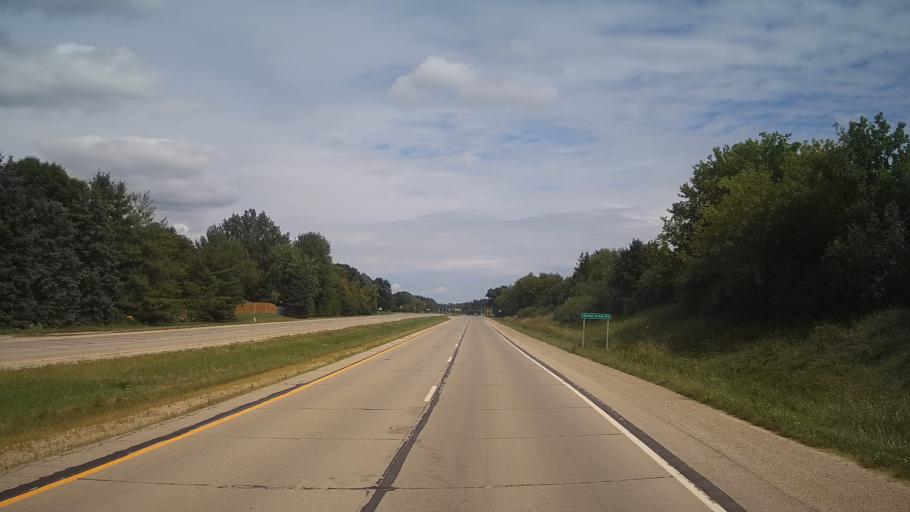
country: US
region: Wisconsin
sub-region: Winnebago County
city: Oshkosh
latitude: 44.0292
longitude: -88.6134
